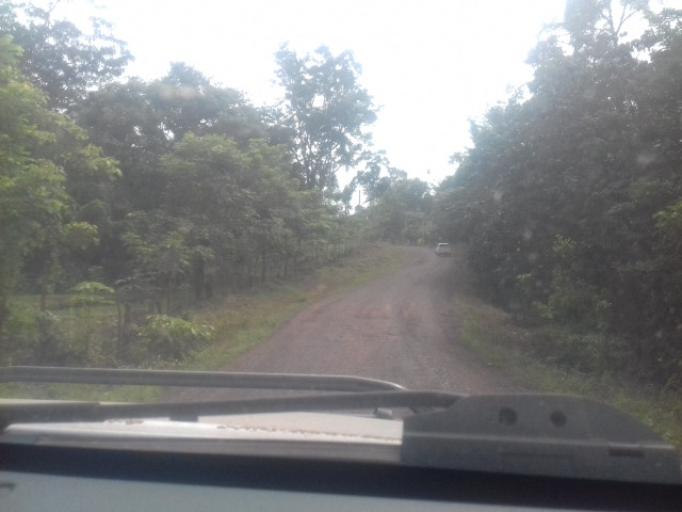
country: NI
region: Atlantico Norte (RAAN)
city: Waslala
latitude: 13.4161
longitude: -85.3189
